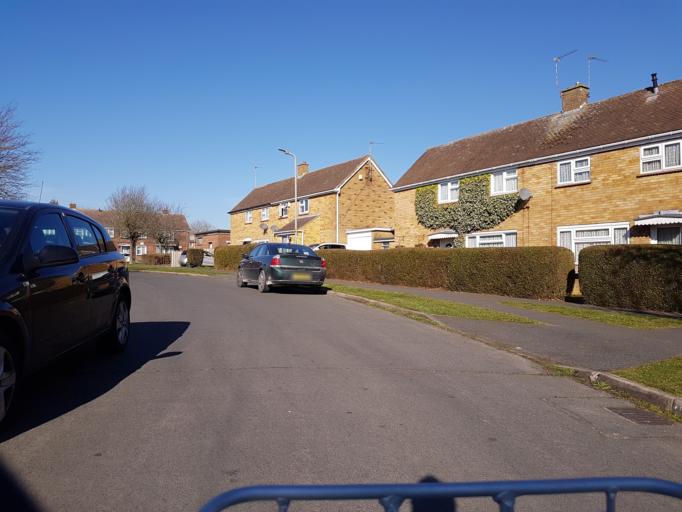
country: GB
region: England
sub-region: Buckinghamshire
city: Newton Longville
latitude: 51.9908
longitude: -0.7630
